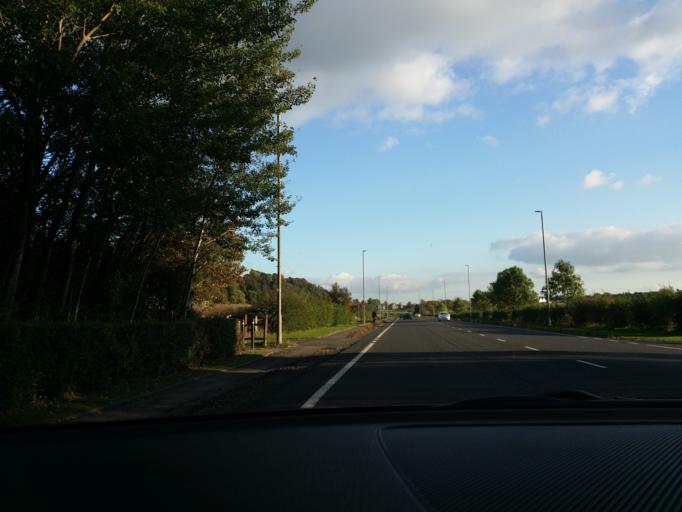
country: GB
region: Scotland
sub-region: Stirling
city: Stirling
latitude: 56.1272
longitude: -3.9608
